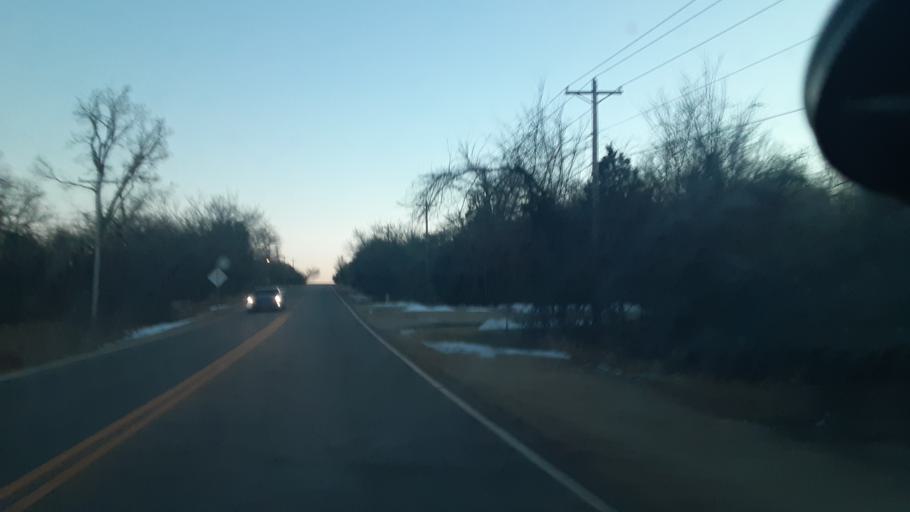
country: US
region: Oklahoma
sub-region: Oklahoma County
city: Edmond
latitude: 35.7095
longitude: -97.4252
